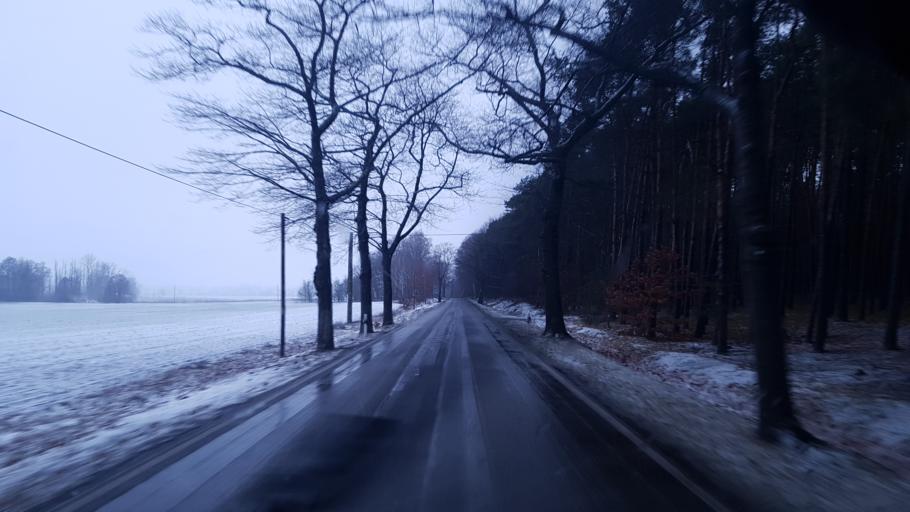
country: DE
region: Brandenburg
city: Tauer
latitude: 51.8961
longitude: 14.4820
